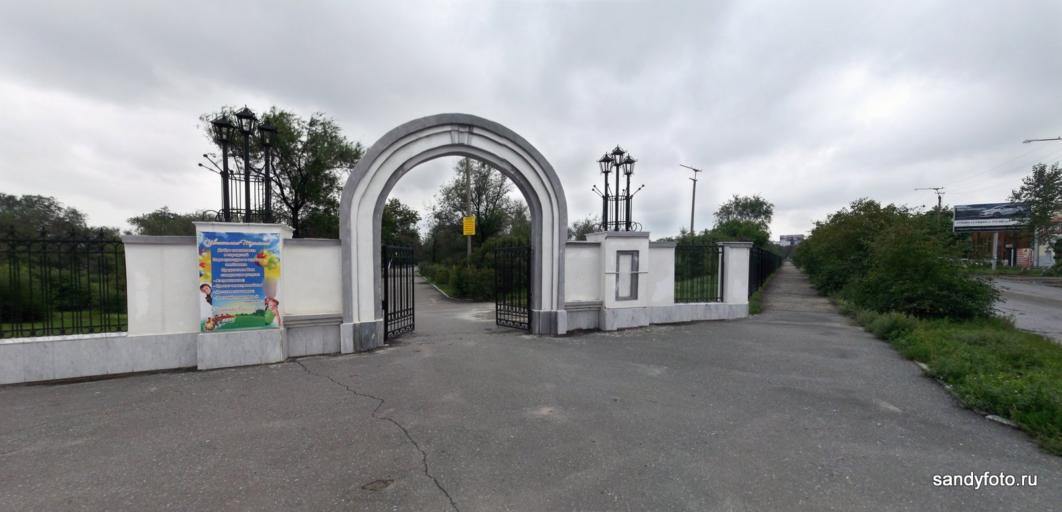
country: RU
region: Chelyabinsk
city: Troitsk
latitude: 54.0853
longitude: 61.5484
